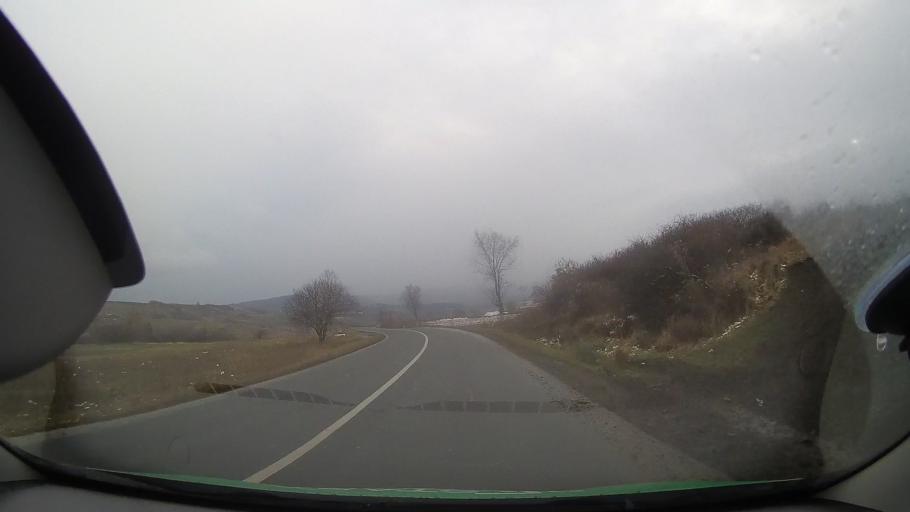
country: RO
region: Sibiu
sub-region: Comuna Blajel
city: Blajel
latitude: 46.2444
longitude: 24.3007
